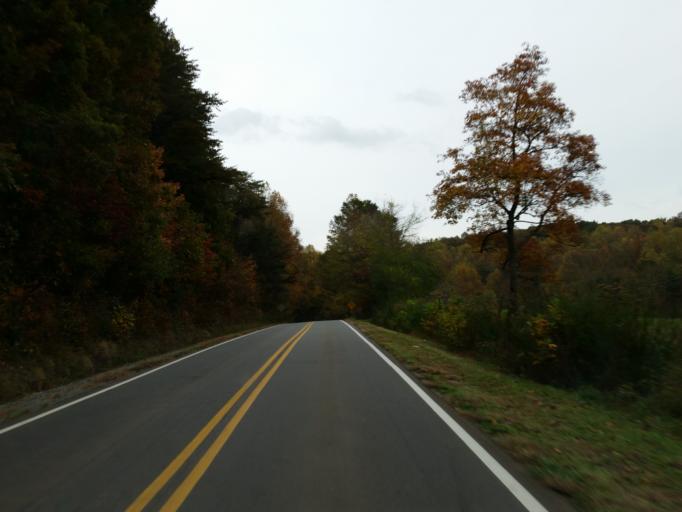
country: US
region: Georgia
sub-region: Gilmer County
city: Ellijay
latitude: 34.6531
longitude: -84.3522
